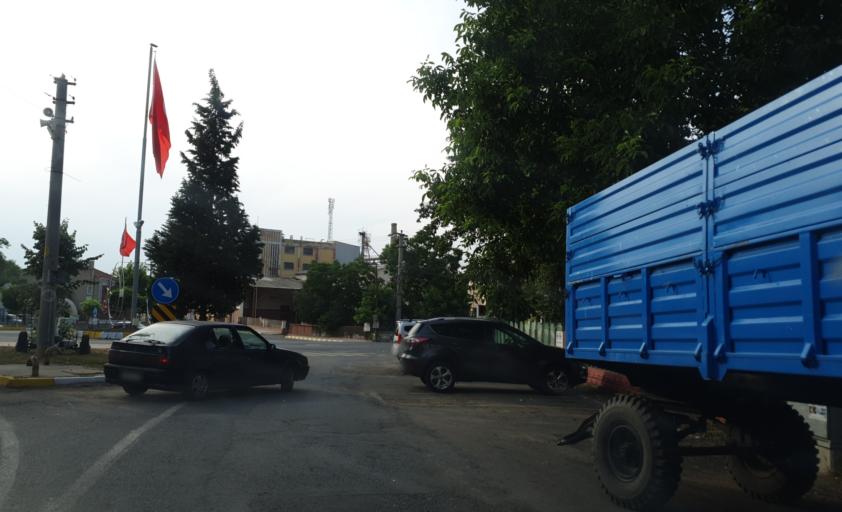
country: TR
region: Tekirdag
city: Hayrabolu
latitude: 41.2174
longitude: 27.1089
